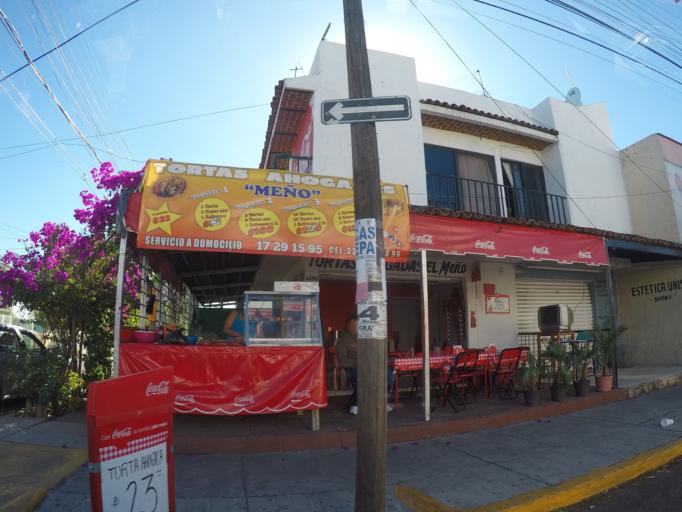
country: MX
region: Jalisco
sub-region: Zapopan
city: Zapopan
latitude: 20.7320
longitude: -103.3504
